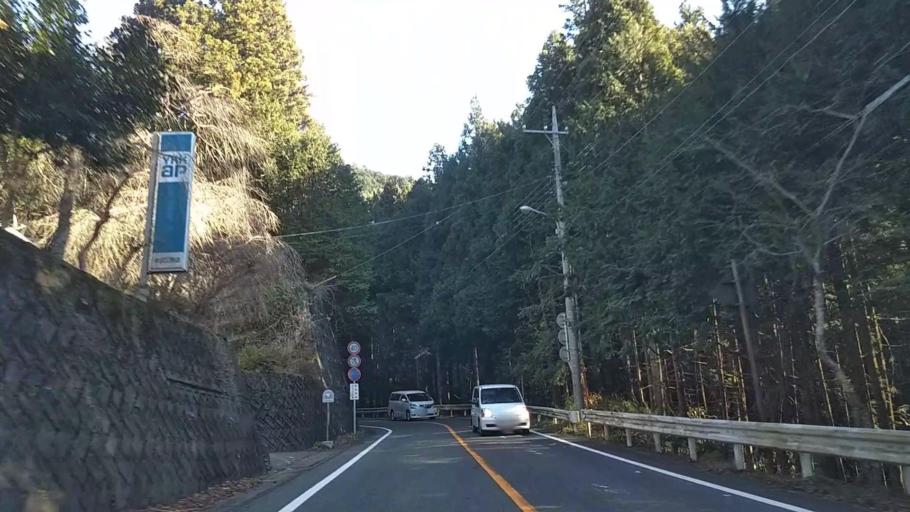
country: JP
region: Yamanashi
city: Uenohara
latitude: 35.5319
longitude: 139.0963
